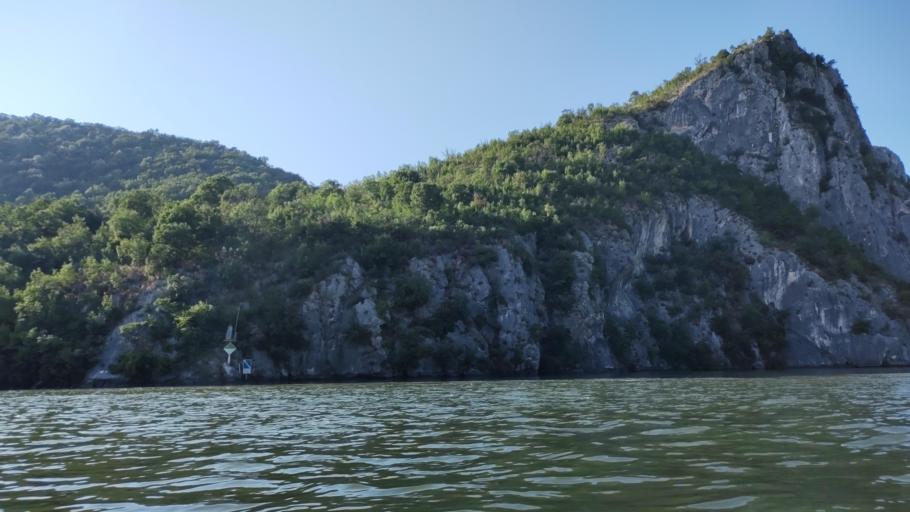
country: RO
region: Mehedinti
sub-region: Comuna Dubova
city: Dubova
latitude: 44.5879
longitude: 22.2562
